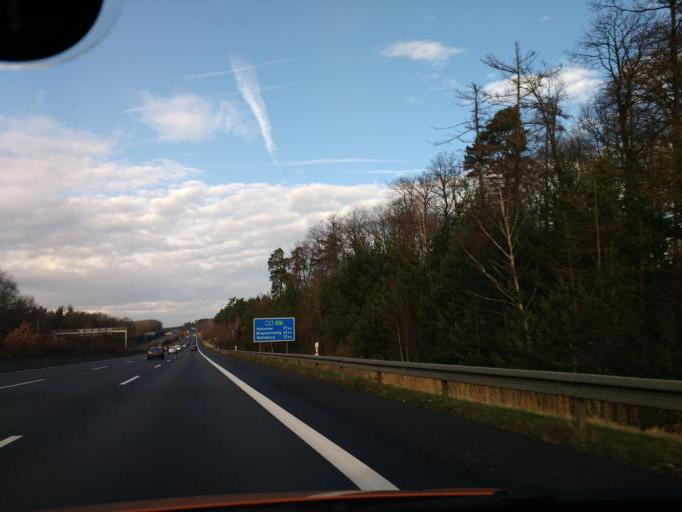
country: DE
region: Lower Saxony
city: Helmstedt
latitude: 52.2484
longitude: 11.0025
